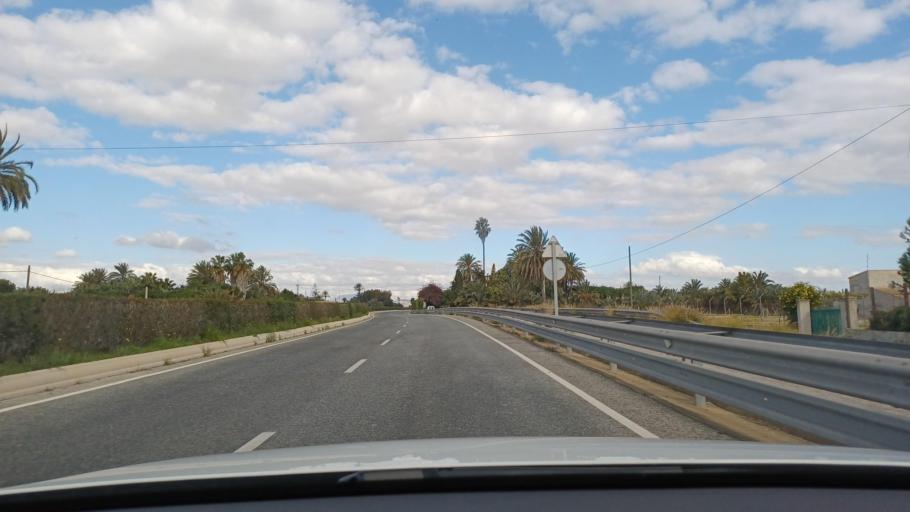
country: ES
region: Valencia
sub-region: Provincia de Alicante
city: Elche
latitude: 38.1977
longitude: -0.7004
